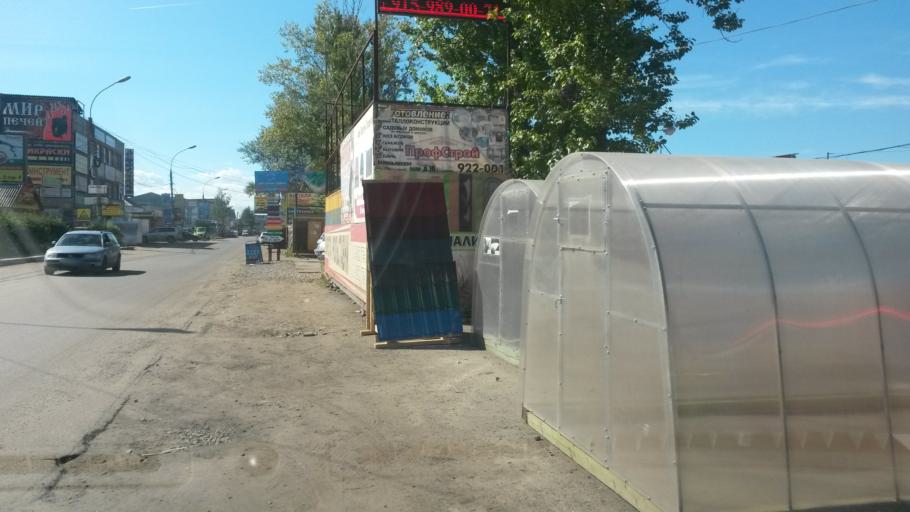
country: RU
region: Jaroslavl
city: Yaroslavl
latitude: 57.6184
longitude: 39.8426
